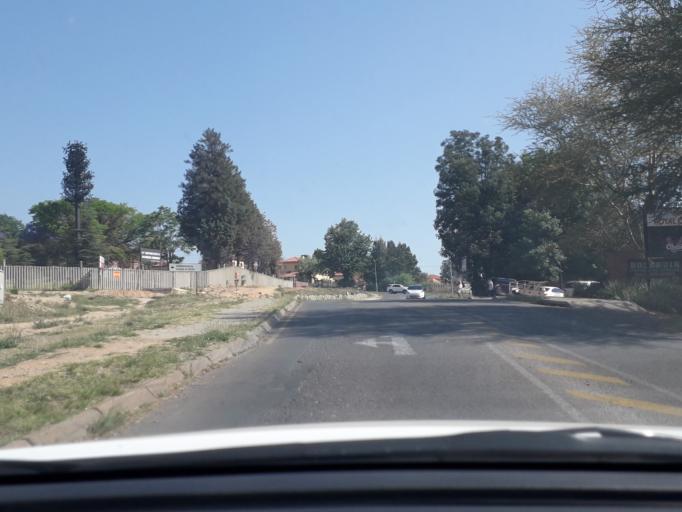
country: ZA
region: Gauteng
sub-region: City of Johannesburg Metropolitan Municipality
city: Roodepoort
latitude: -26.0820
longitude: 27.9452
